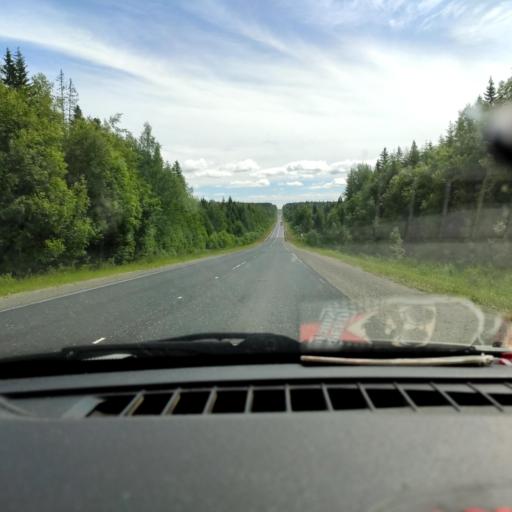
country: RU
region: Perm
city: Chusovoy
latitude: 58.3741
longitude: 57.9725
